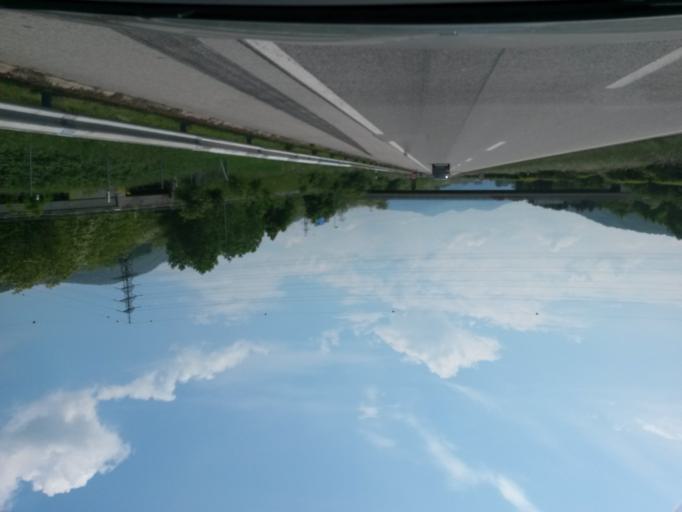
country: CH
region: Ticino
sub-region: Lugano District
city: Cadempino
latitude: 46.0297
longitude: 8.9258
